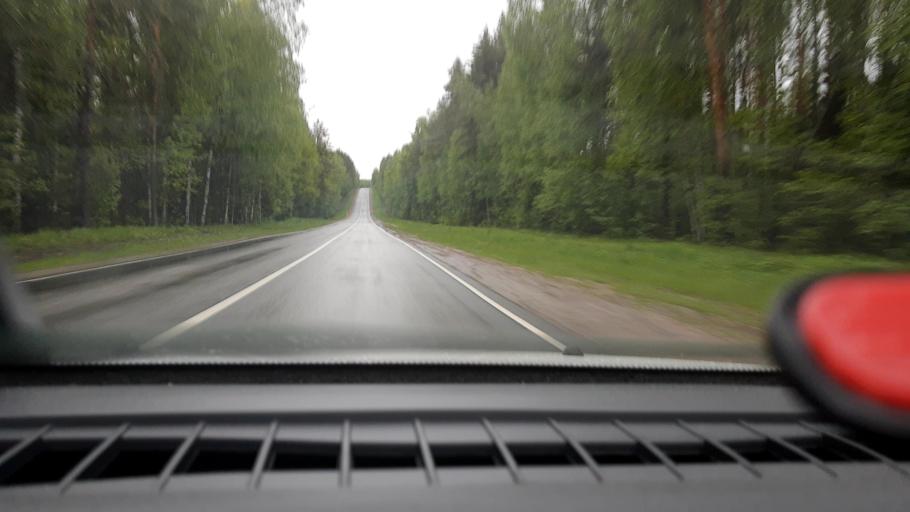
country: RU
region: Nizjnij Novgorod
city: Krasnyye Baki
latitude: 56.9928
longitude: 45.1147
